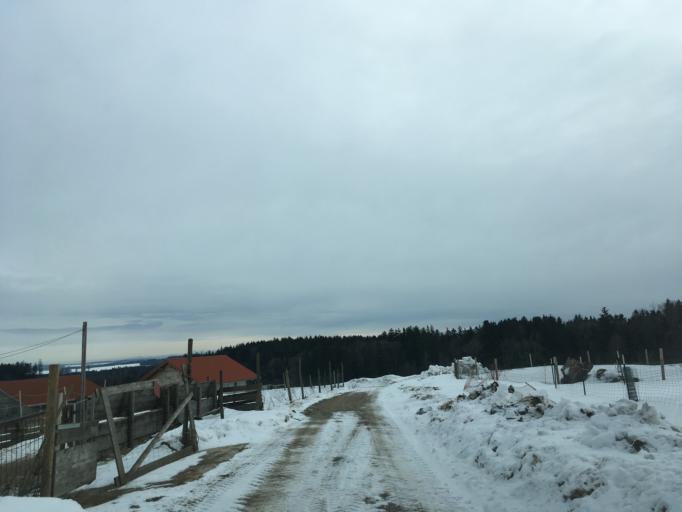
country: DE
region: Bavaria
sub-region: Upper Bavaria
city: Schnaitsee
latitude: 48.0826
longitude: 12.3776
